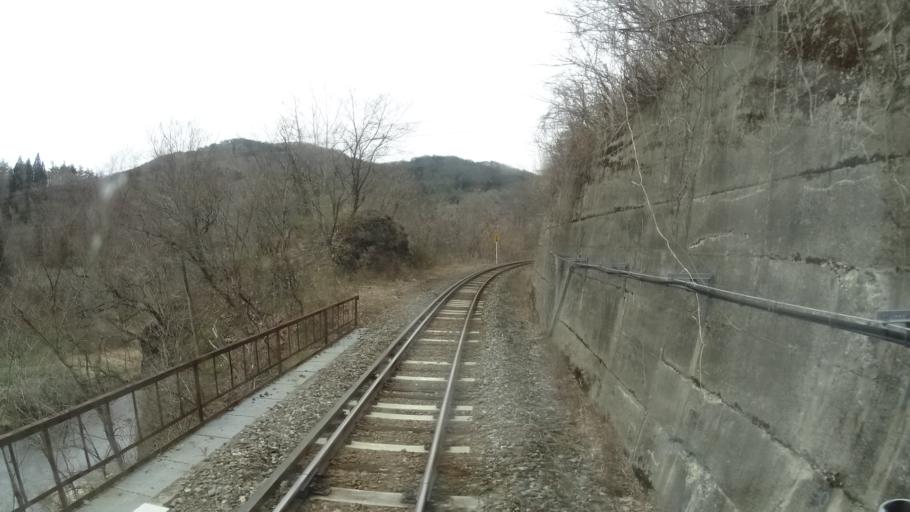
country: JP
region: Iwate
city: Hanamaki
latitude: 39.3563
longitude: 141.3214
